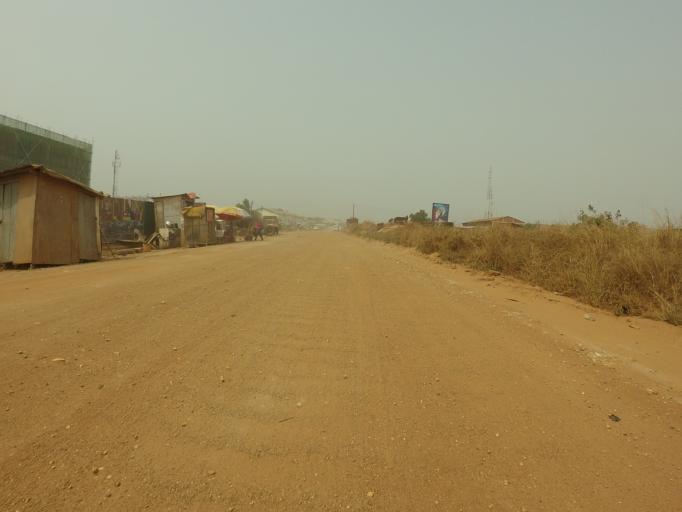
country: GH
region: Greater Accra
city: Medina Estates
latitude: 5.6352
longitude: -0.1255
